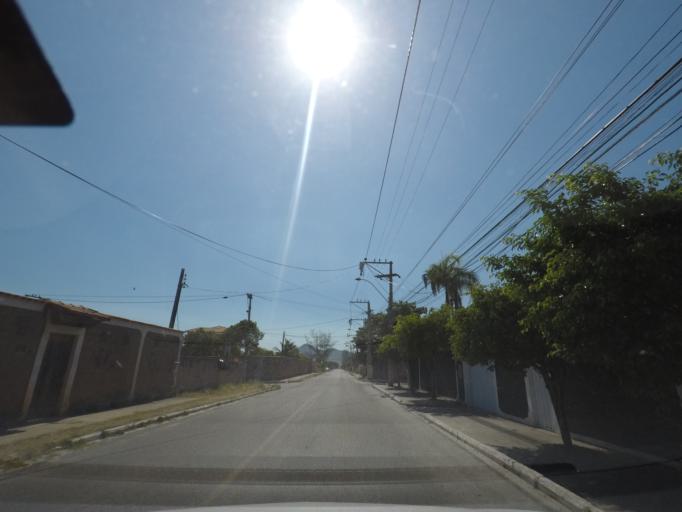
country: BR
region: Rio de Janeiro
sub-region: Marica
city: Marica
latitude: -22.9671
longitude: -42.9537
